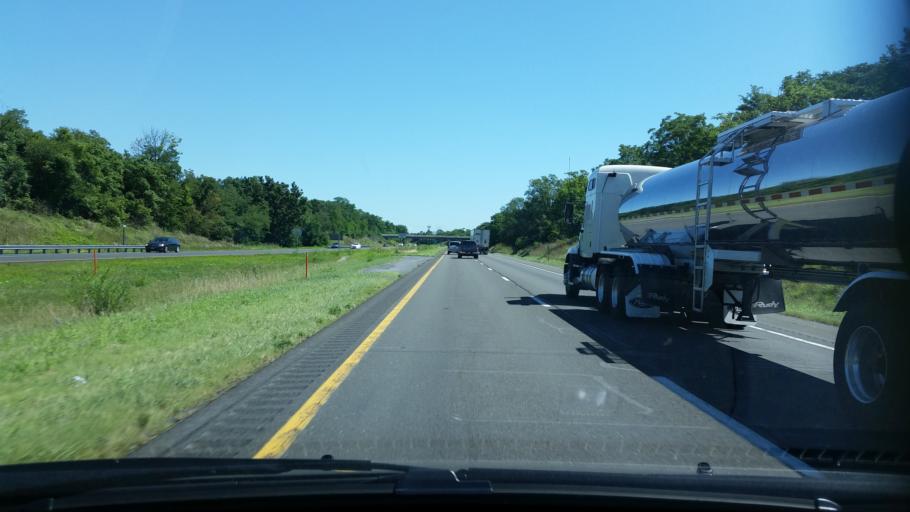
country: US
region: Virginia
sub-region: City of Winchester
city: Winchester
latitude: 39.1767
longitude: -78.1462
